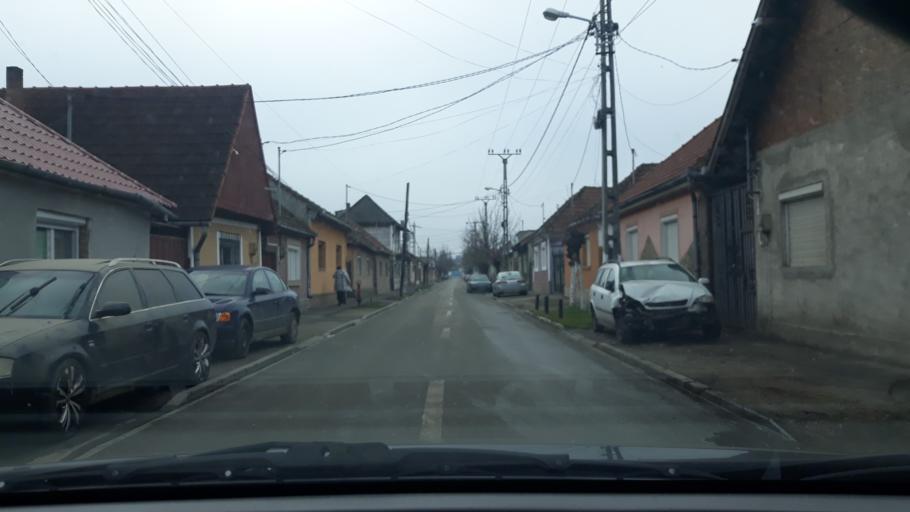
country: RO
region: Bihor
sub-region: Comuna Biharea
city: Oradea
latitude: 47.0488
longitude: 21.9693
